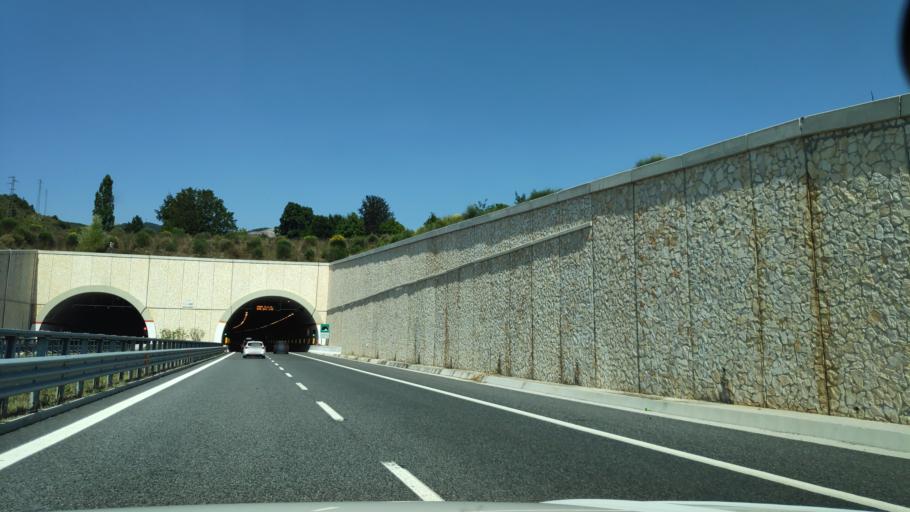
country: IT
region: Calabria
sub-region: Provincia di Cosenza
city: Mormanno
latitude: 39.8851
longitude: 16.0525
